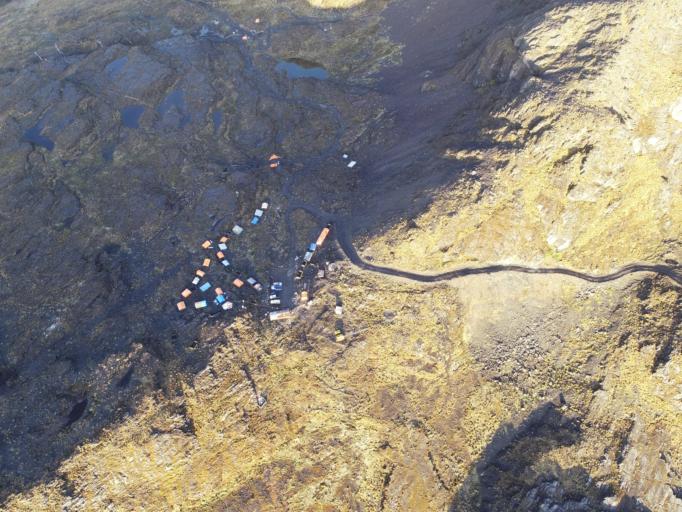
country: PE
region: Puno
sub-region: San Antonio De Putina
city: Sina
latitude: -14.7392
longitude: -69.0480
